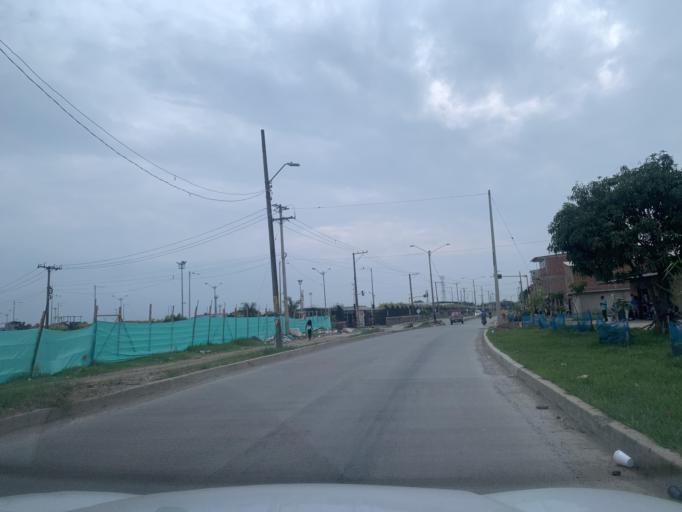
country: CO
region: Valle del Cauca
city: Cali
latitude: 3.4106
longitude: -76.4781
